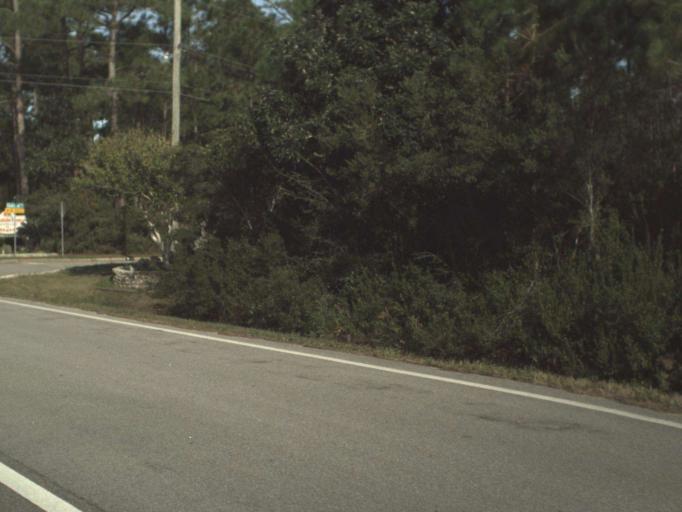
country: US
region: Florida
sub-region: Escambia County
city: Myrtle Grove
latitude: 30.3345
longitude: -87.4120
